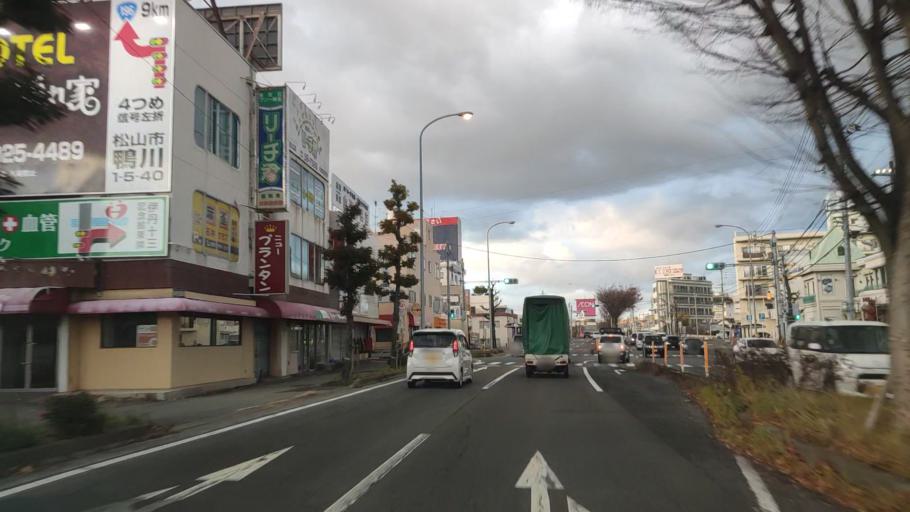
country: JP
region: Ehime
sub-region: Shikoku-chuo Shi
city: Matsuyama
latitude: 33.8162
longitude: 132.7771
